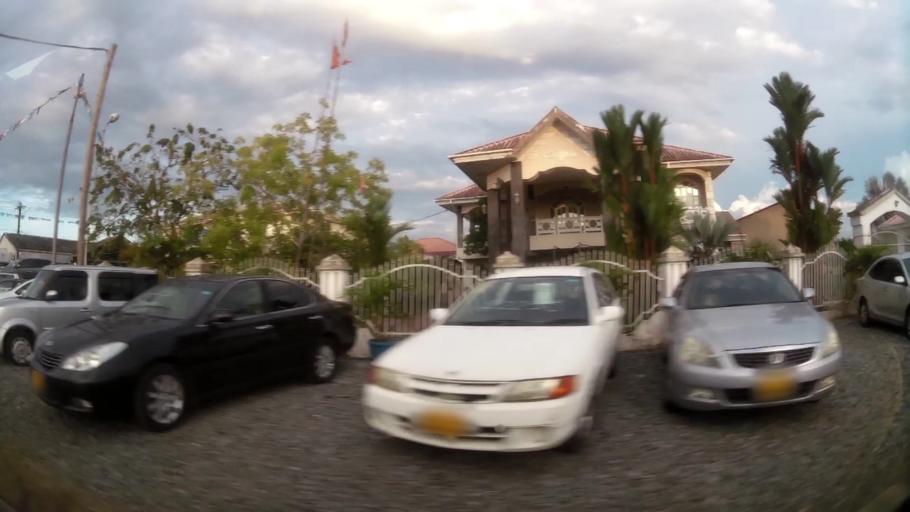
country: SR
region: Paramaribo
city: Paramaribo
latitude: 5.7787
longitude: -55.1679
